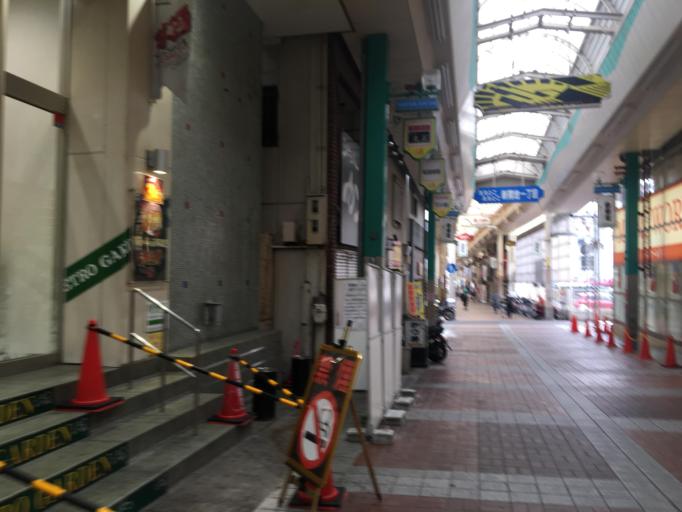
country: JP
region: Hyogo
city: Kobe
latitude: 34.6781
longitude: 135.1689
